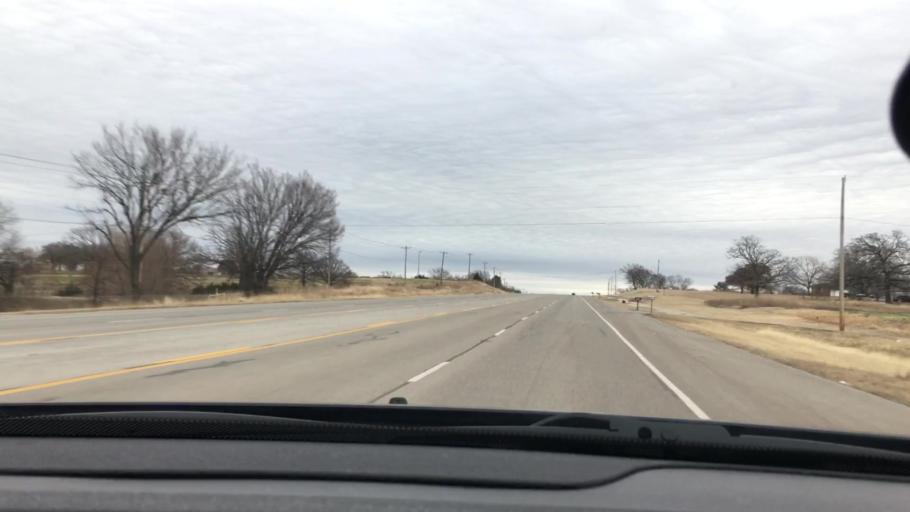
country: US
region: Oklahoma
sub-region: Carter County
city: Dickson
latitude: 34.1871
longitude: -97.0260
